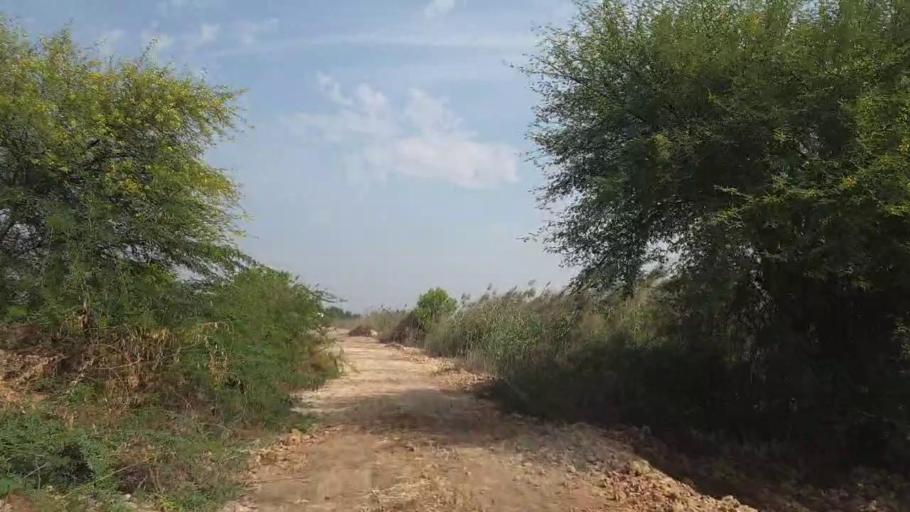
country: PK
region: Sindh
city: Rajo Khanani
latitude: 24.9975
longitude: 69.0020
